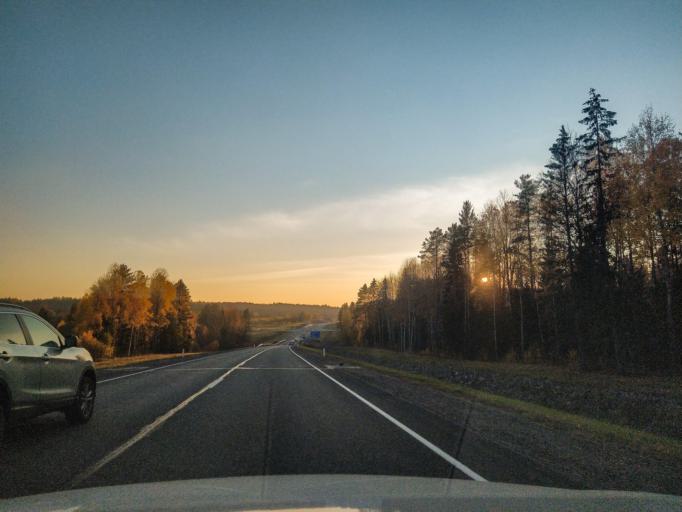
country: RU
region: Leningrad
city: Kuznechnoye
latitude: 61.3421
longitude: 29.8673
